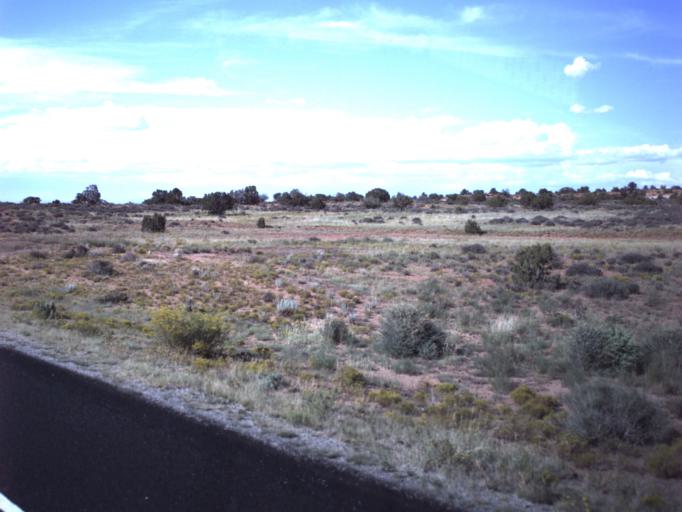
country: US
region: Utah
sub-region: Grand County
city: Moab
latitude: 38.6012
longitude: -109.8155
